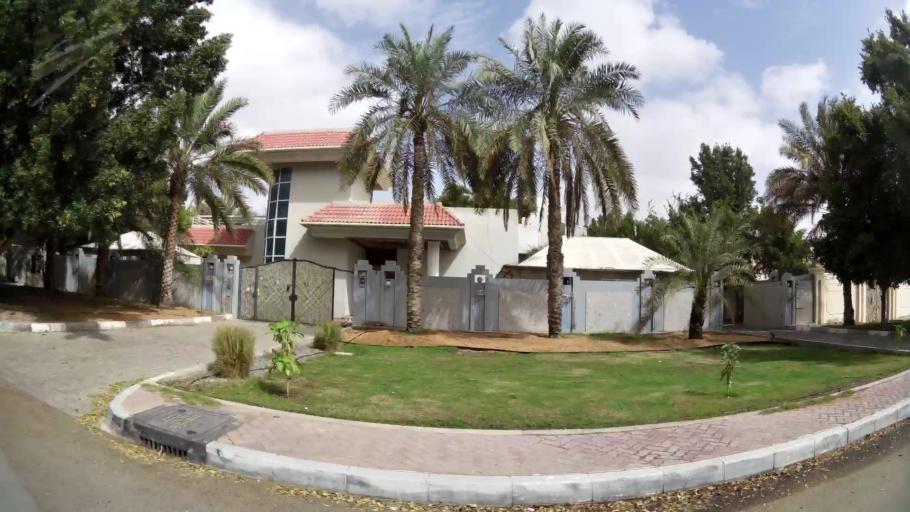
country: AE
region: Abu Dhabi
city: Abu Dhabi
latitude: 24.4037
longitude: 54.5186
